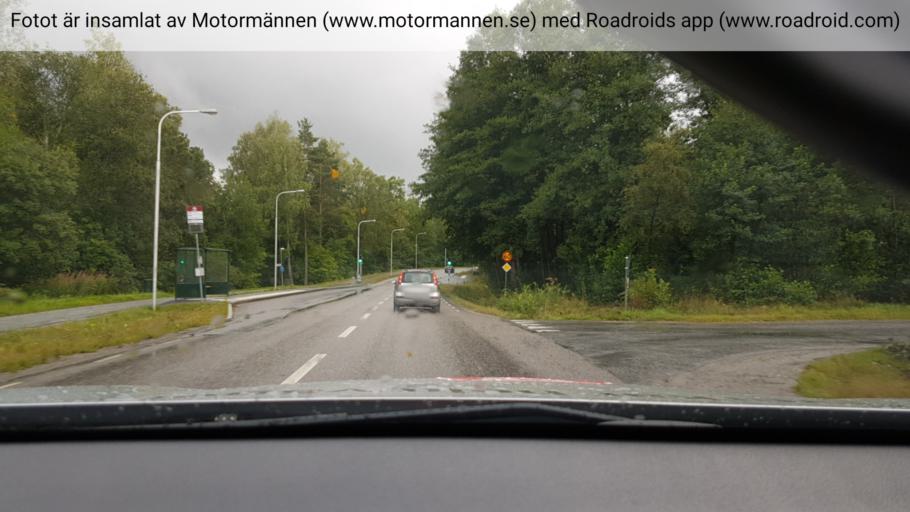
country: SE
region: Stockholm
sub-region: Haninge Kommun
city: Jordbro
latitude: 59.1155
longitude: 18.0608
